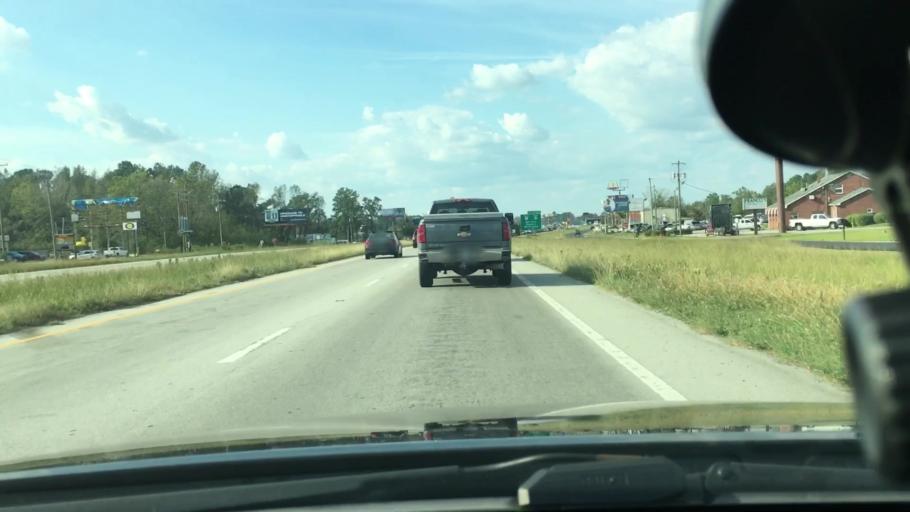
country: US
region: North Carolina
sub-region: Craven County
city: James City
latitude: 35.0774
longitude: -77.0292
